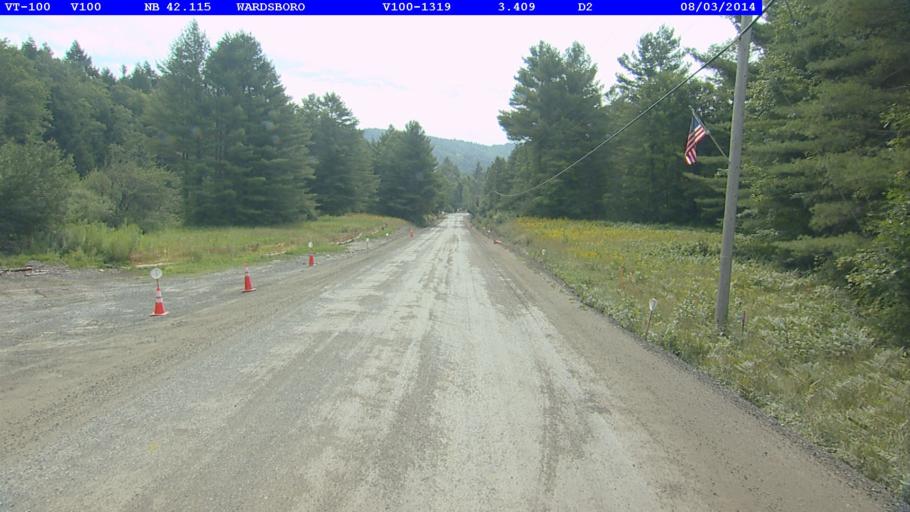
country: US
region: Vermont
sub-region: Windham County
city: Dover
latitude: 43.0292
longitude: -72.8345
